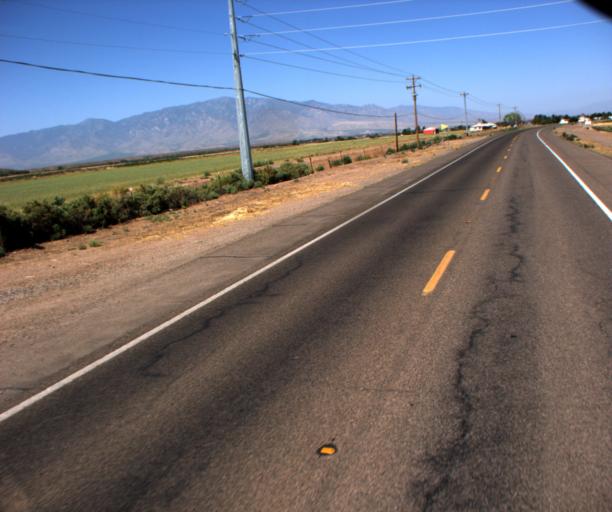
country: US
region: Arizona
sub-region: Graham County
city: Safford
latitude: 32.8129
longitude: -109.6139
